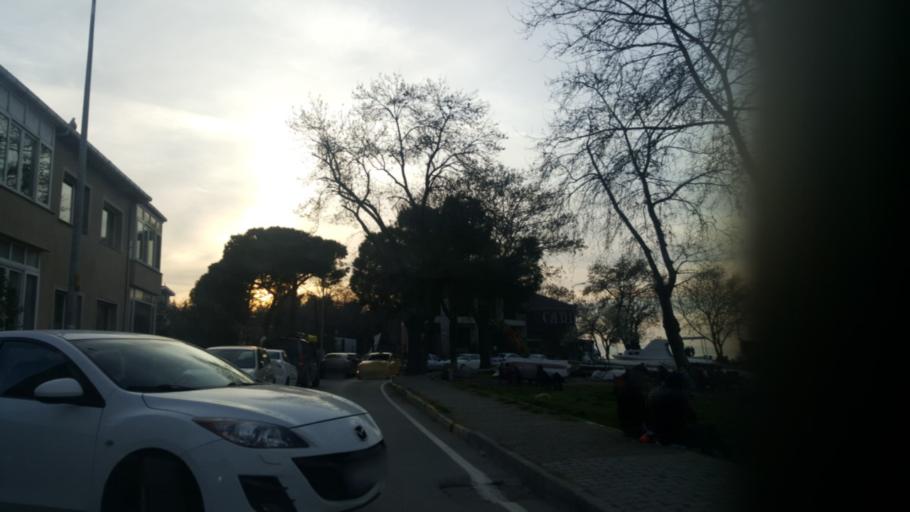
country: TR
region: Istanbul
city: Icmeler
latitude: 40.8199
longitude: 29.2740
